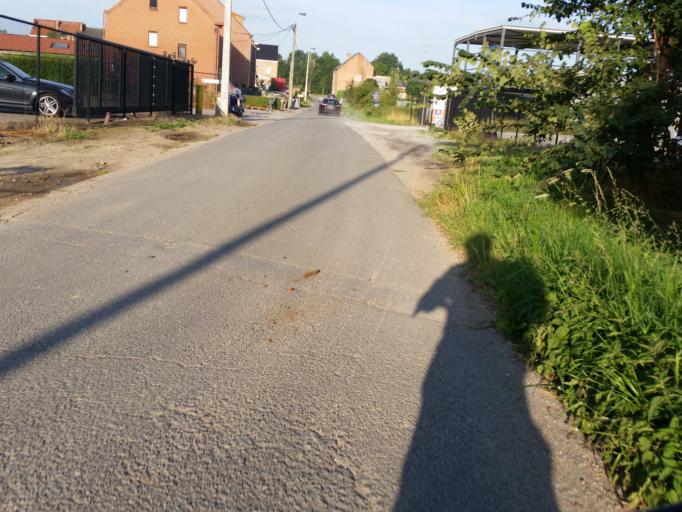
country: BE
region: Flanders
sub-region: Provincie Vlaams-Brabant
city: Vilvoorde
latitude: 50.9568
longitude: 4.4114
